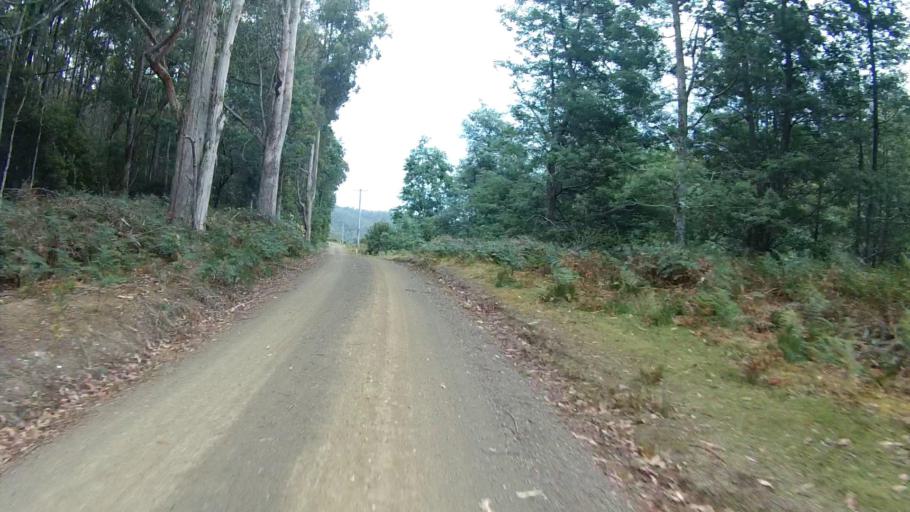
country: AU
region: Tasmania
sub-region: Kingborough
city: Kettering
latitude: -43.2137
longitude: 147.1780
